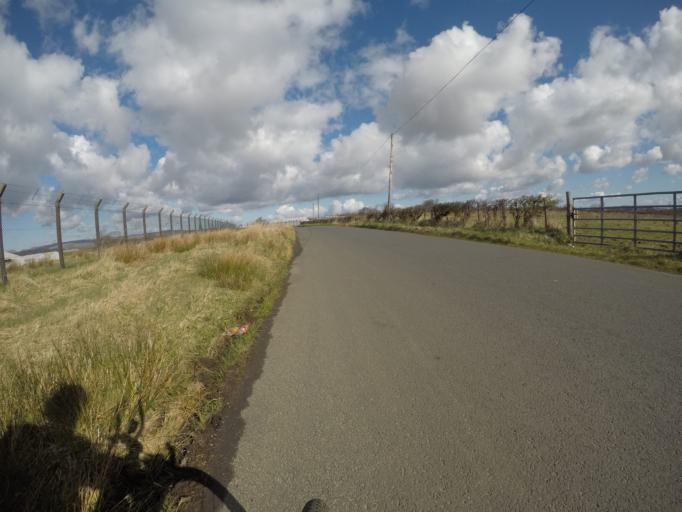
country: GB
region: Scotland
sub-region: North Ayrshire
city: Beith
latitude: 55.7238
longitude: -4.6092
